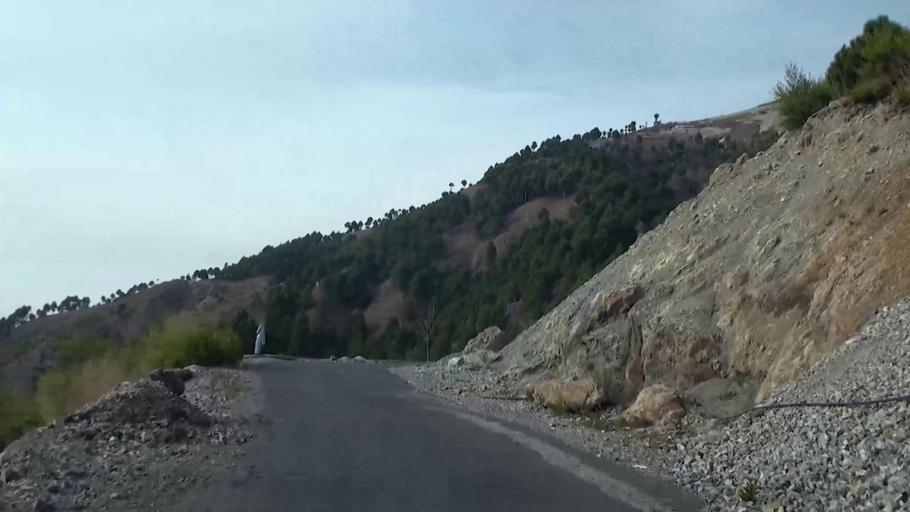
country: PK
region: Azad Kashmir
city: Muzaffarabad
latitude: 34.3656
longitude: 73.5006
